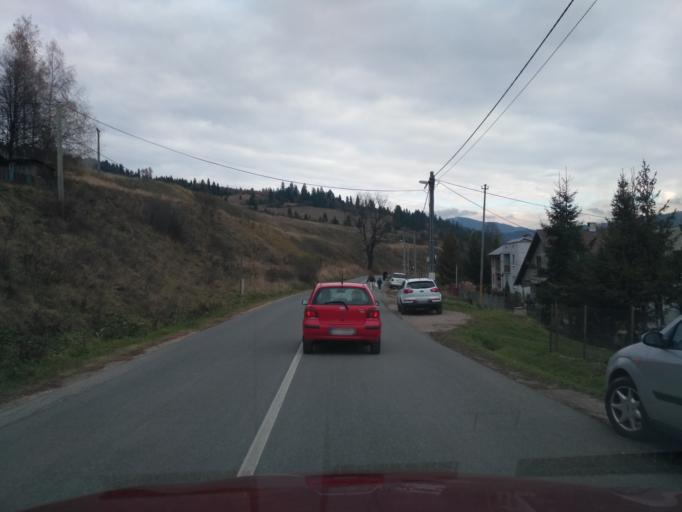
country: SK
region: Kosicky
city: Krompachy
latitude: 48.8113
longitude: 20.7192
